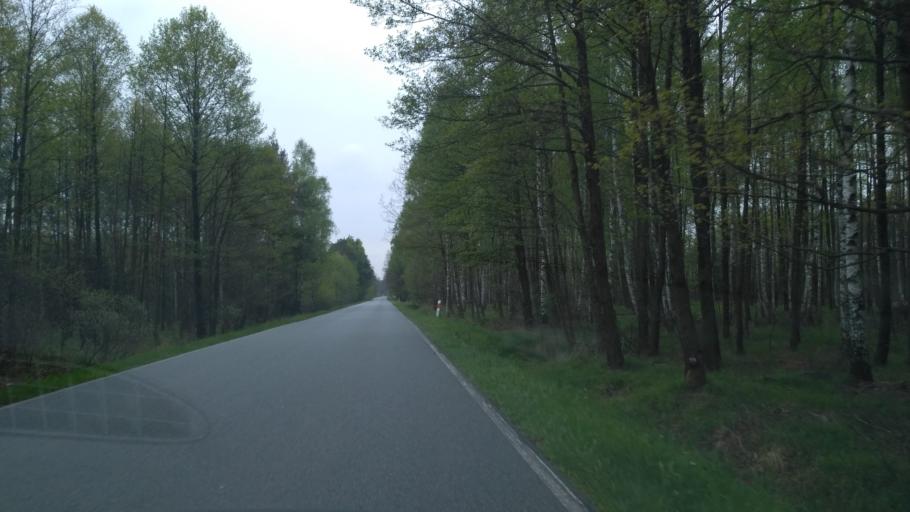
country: PL
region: Subcarpathian Voivodeship
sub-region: Powiat kolbuszowski
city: Kolbuszowa
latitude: 50.1575
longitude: 21.7587
